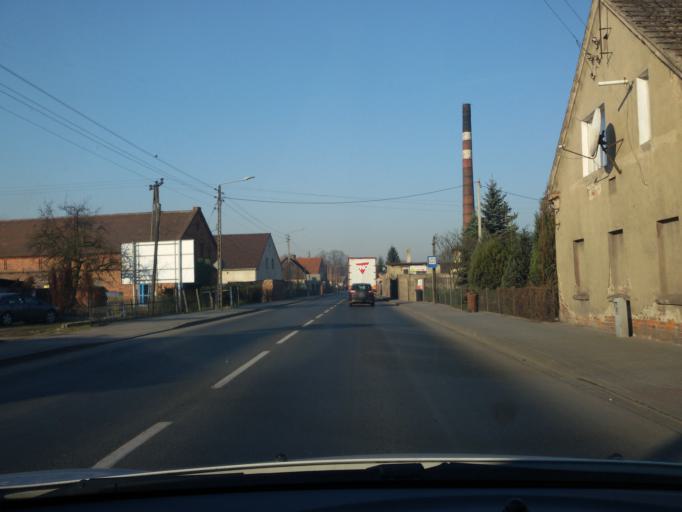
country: PL
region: Lubusz
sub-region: Powiat wschowski
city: Wschowa
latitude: 51.8022
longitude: 16.3247
